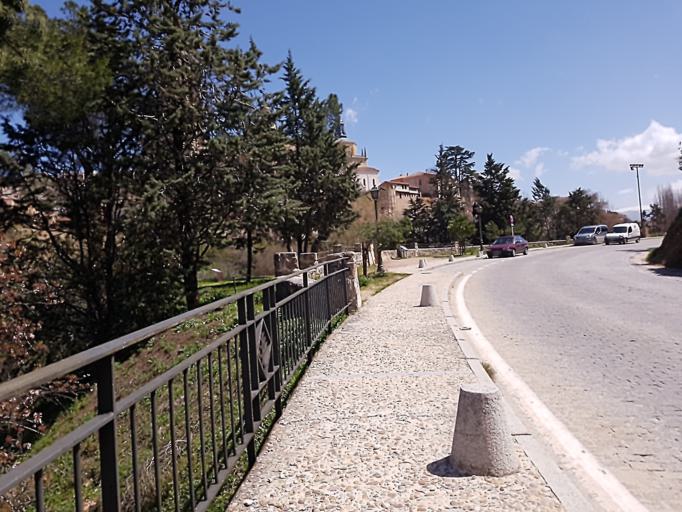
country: ES
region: Castille and Leon
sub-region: Provincia de Segovia
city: Segovia
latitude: 40.9491
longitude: -4.1288
